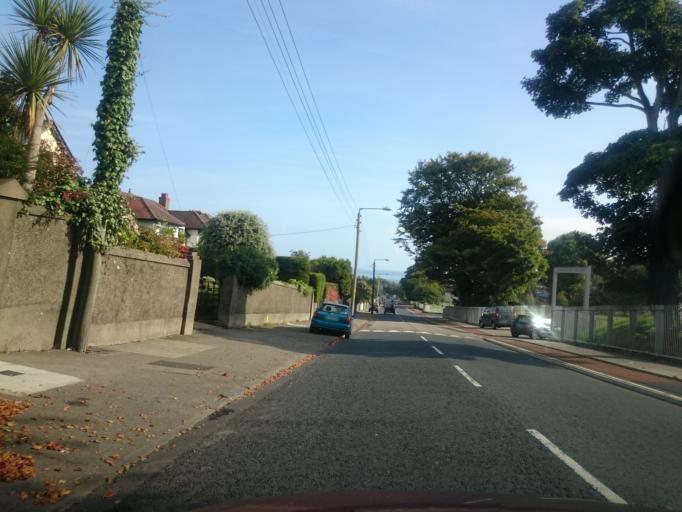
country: IE
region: Leinster
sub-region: Wicklow
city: Bray
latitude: 53.1938
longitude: -6.1037
